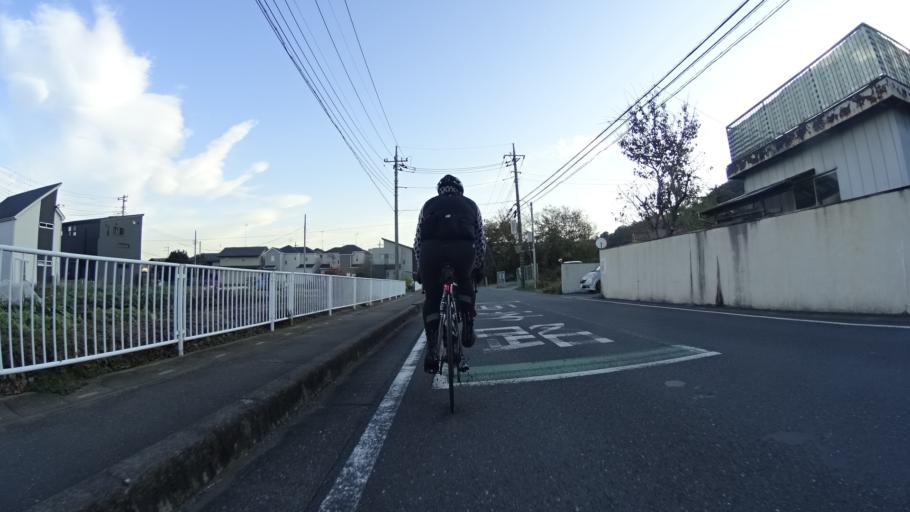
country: JP
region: Saitama
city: Hanno
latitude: 35.8436
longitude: 139.3172
